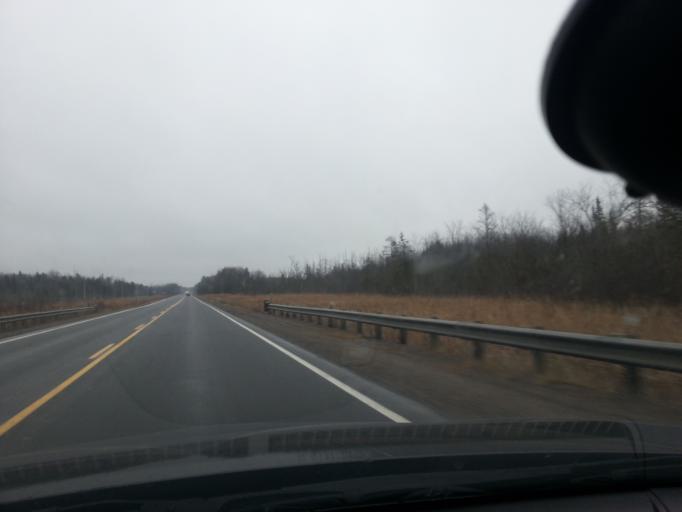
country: CA
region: Ontario
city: Belleville
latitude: 44.5270
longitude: -77.4099
